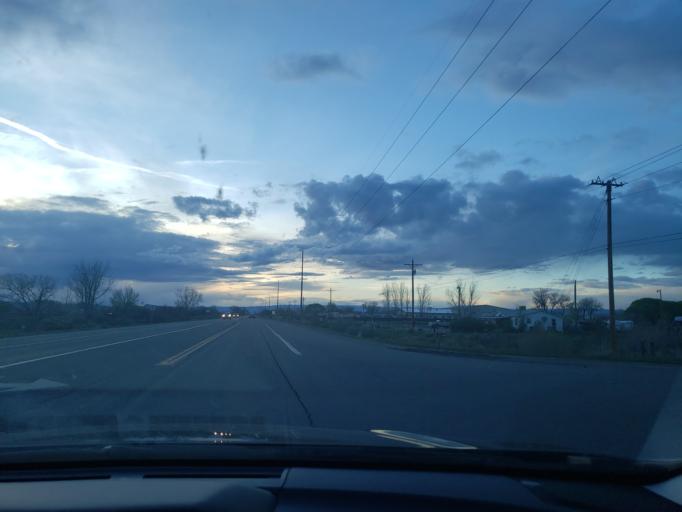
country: US
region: Colorado
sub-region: Mesa County
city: Fruita
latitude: 39.1295
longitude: -108.6826
